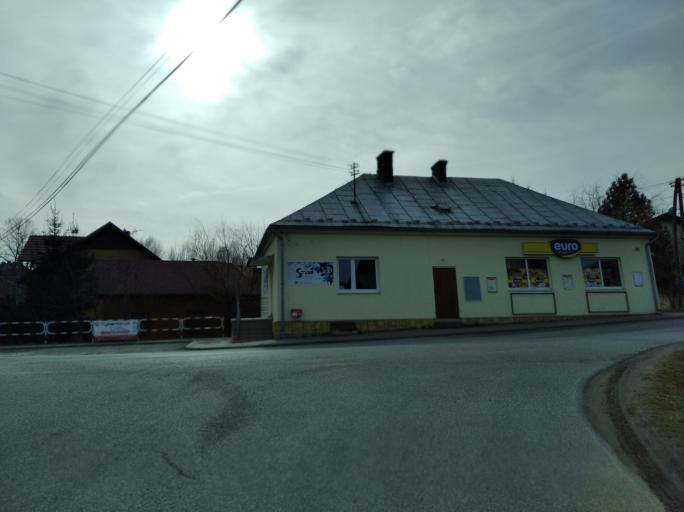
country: PL
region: Subcarpathian Voivodeship
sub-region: Powiat brzozowski
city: Orzechowka
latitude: 49.7294
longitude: 21.9448
